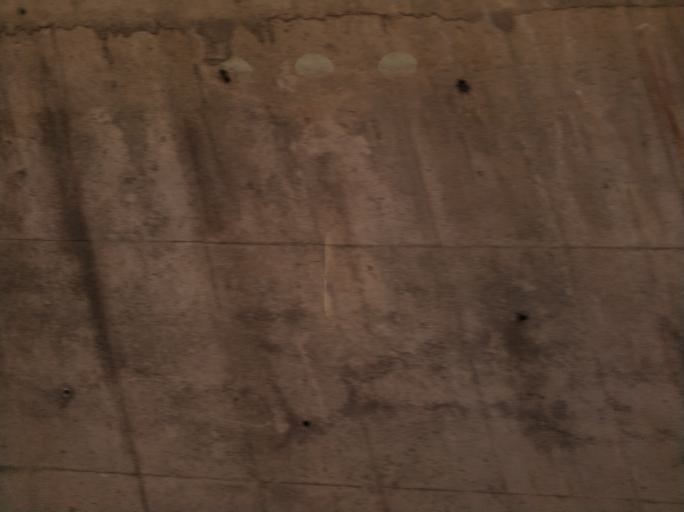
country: IR
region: Gilan
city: Pa'in-e Bazar-e Rudbar
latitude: 36.9863
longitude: 49.5592
